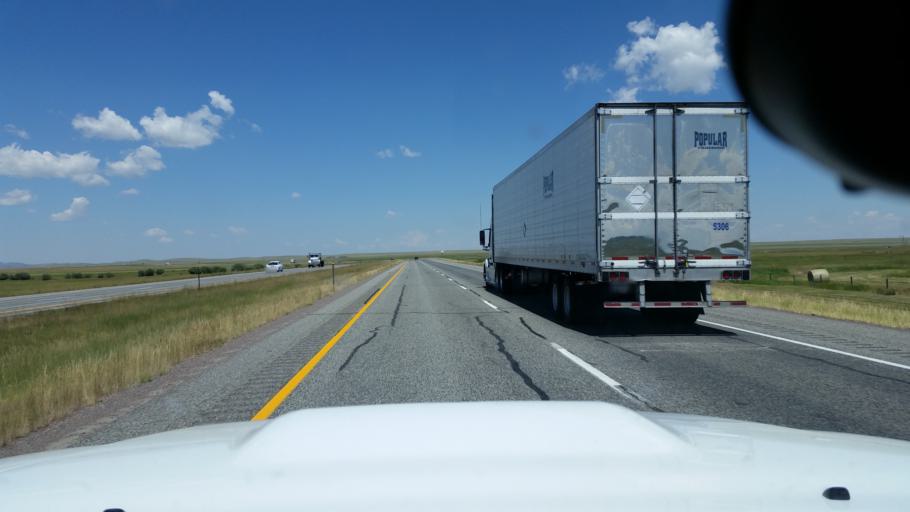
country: US
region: Wyoming
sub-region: Albany County
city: Laramie
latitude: 41.4047
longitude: -105.8322
